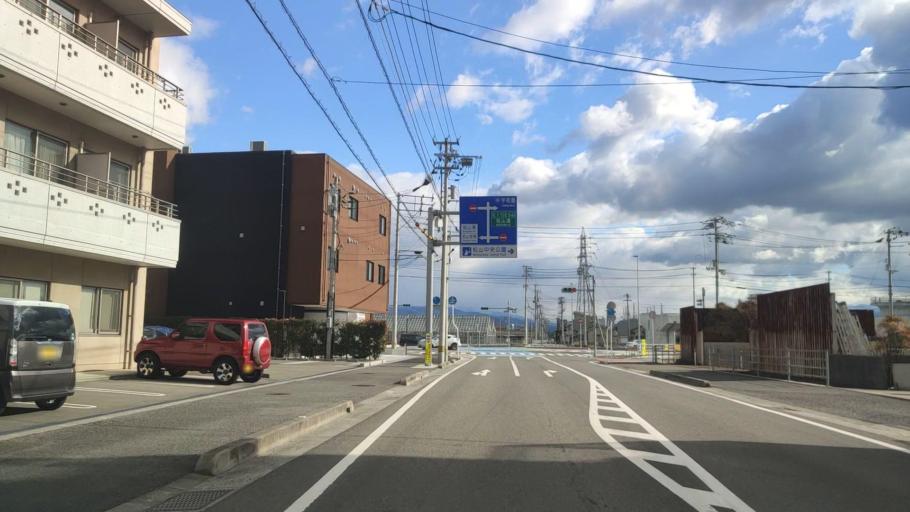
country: JP
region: Ehime
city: Masaki-cho
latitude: 33.8174
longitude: 132.7185
